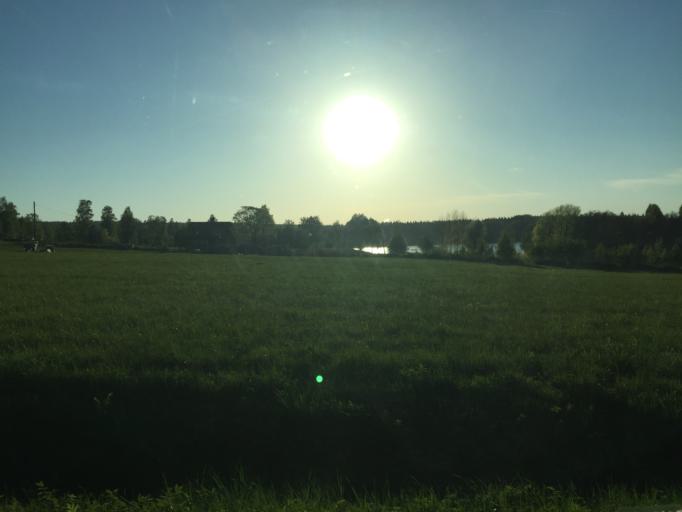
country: SE
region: Soedermanland
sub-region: Vingakers Kommun
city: Vingaker
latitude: 58.9984
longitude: 15.6760
